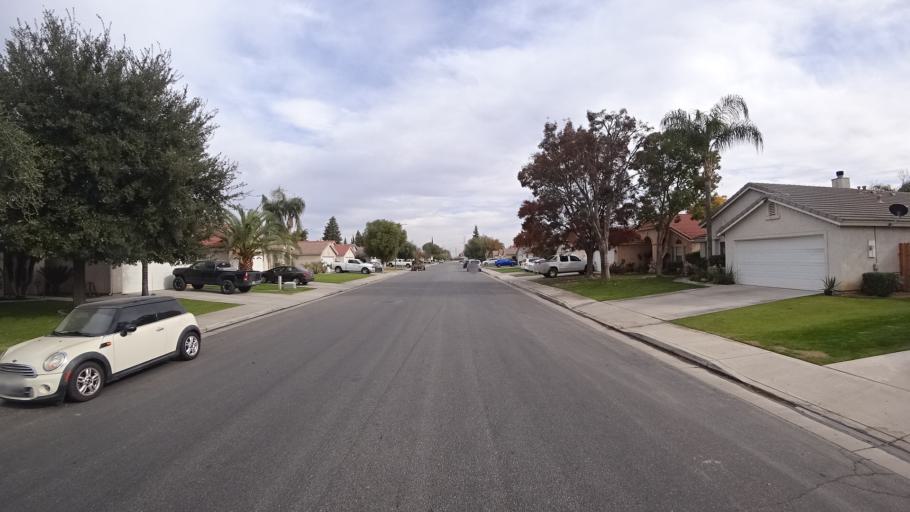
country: US
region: California
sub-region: Kern County
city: Greenacres
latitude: 35.3907
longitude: -119.0997
